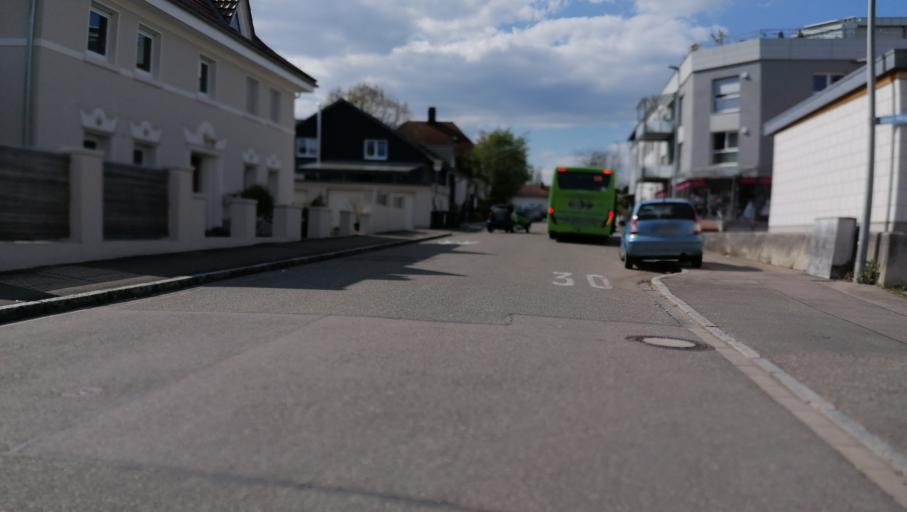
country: DE
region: Baden-Wuerttemberg
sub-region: Freiburg Region
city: Bad Sackingen
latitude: 47.5501
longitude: 7.9395
